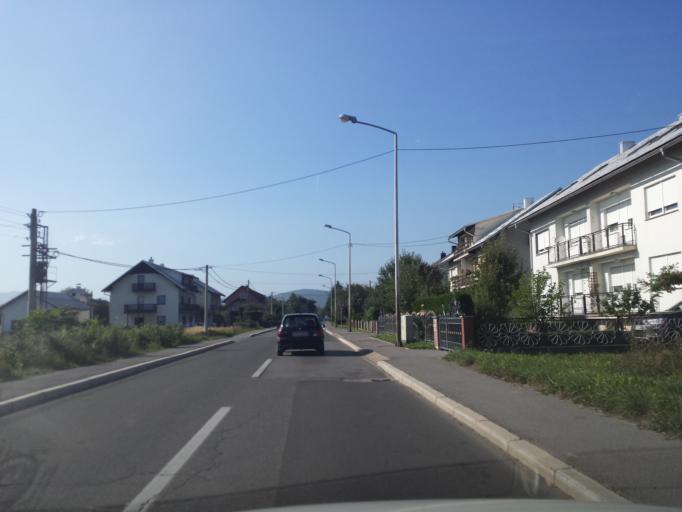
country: HR
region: Karlovacka
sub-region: Grad Ogulin
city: Ogulin
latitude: 45.2520
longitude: 15.2387
